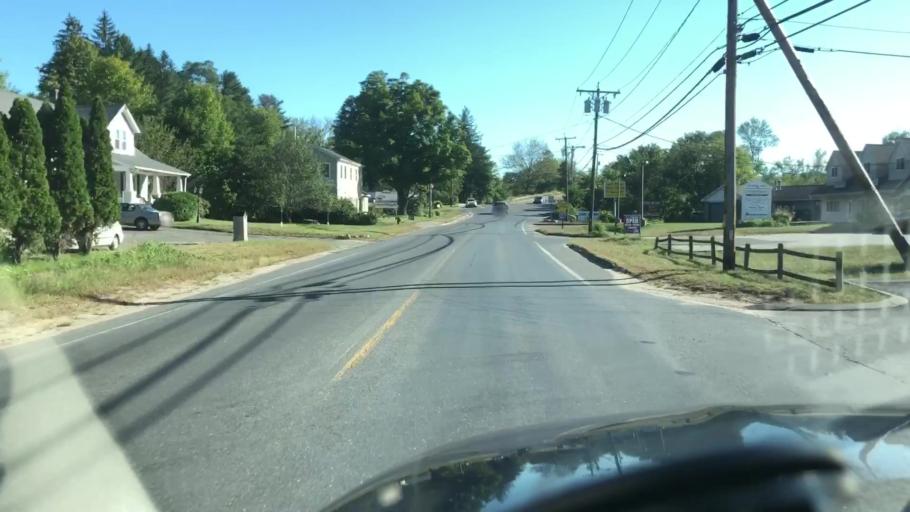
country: US
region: Massachusetts
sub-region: Hampden County
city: Monson
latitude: 42.1265
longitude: -72.3066
